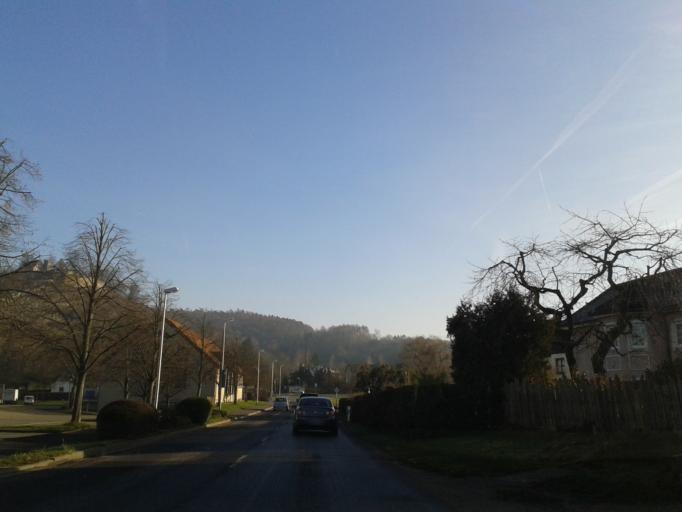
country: DE
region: Bavaria
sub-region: Regierungsbezirk Unterfranken
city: Hassfurt
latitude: 50.0793
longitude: 10.5673
